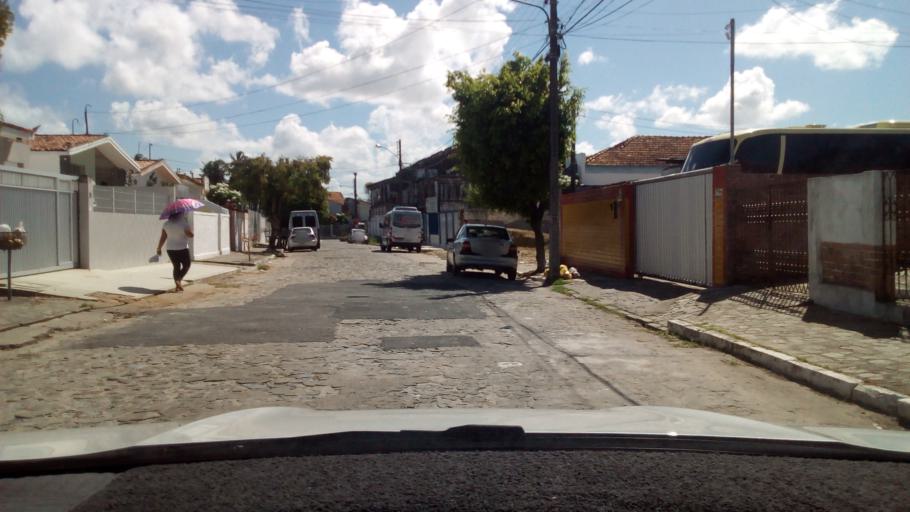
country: BR
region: Paraiba
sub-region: Joao Pessoa
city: Joao Pessoa
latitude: -7.1279
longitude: -34.8832
